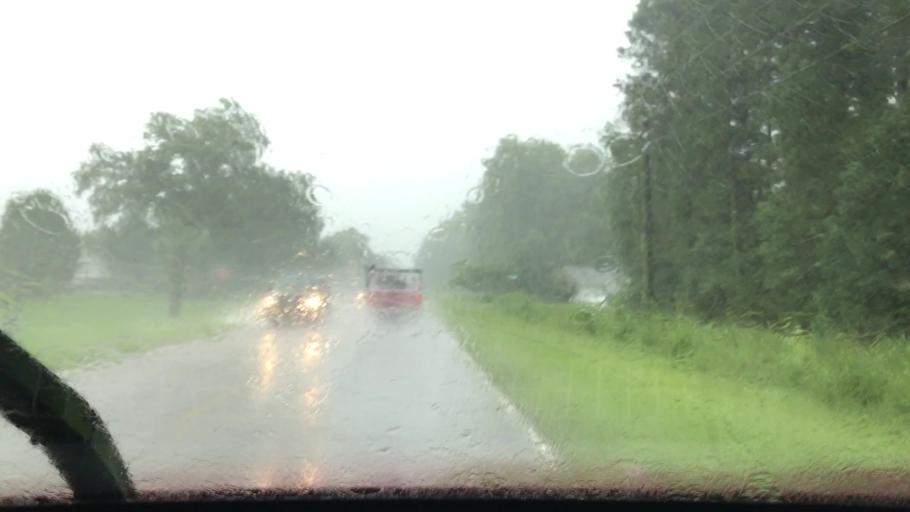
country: US
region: South Carolina
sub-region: Horry County
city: Red Hill
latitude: 33.8660
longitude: -78.9878
